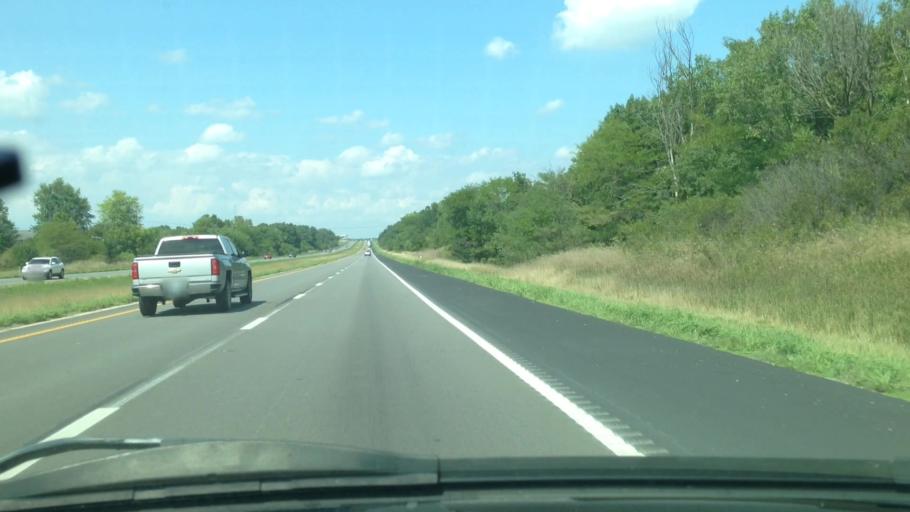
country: US
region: Missouri
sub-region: Lincoln County
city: Troy
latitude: 39.0510
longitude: -90.9739
